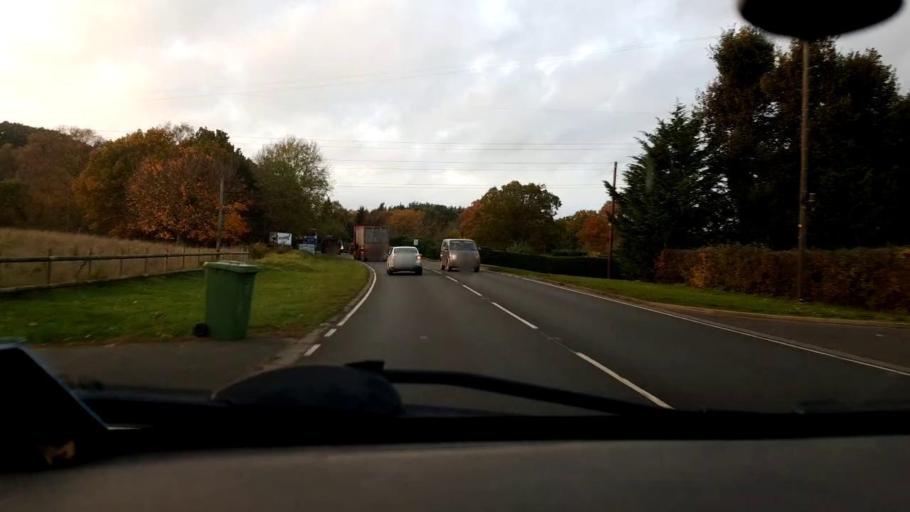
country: GB
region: England
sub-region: Norfolk
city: Costessey
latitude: 52.7109
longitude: 1.1401
